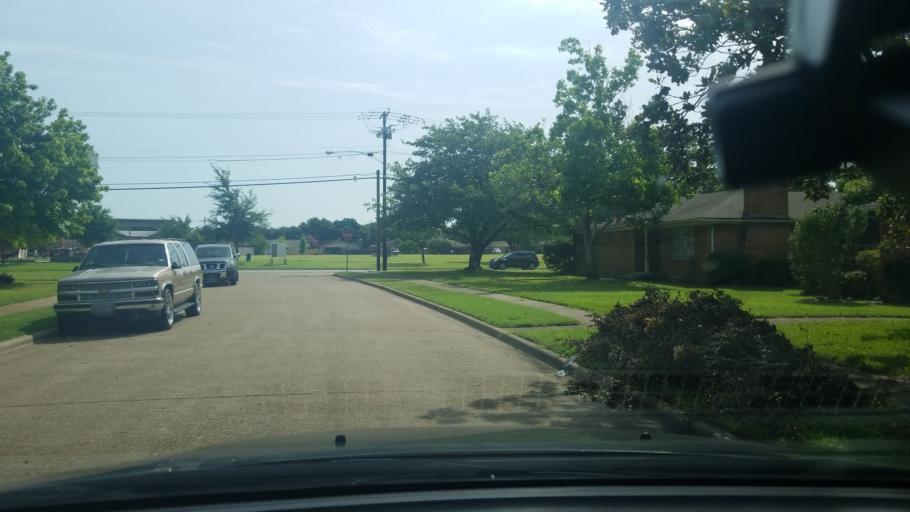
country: US
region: Texas
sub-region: Dallas County
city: Highland Park
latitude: 32.8032
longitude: -96.6979
